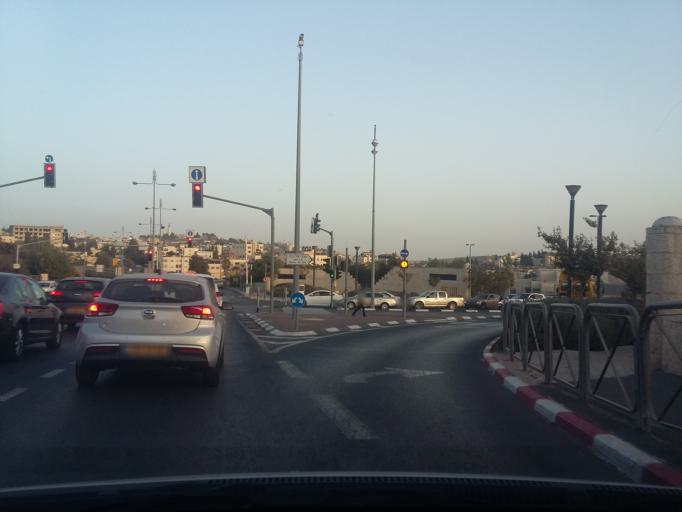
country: PS
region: West Bank
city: East Jerusalem
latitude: 31.7956
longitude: 35.2357
